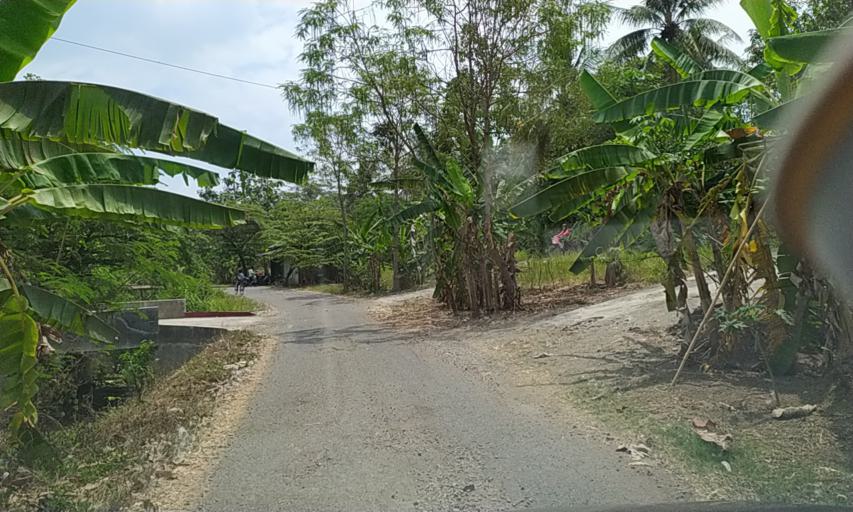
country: ID
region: Central Java
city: Cipariuk
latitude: -7.4985
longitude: 108.7615
